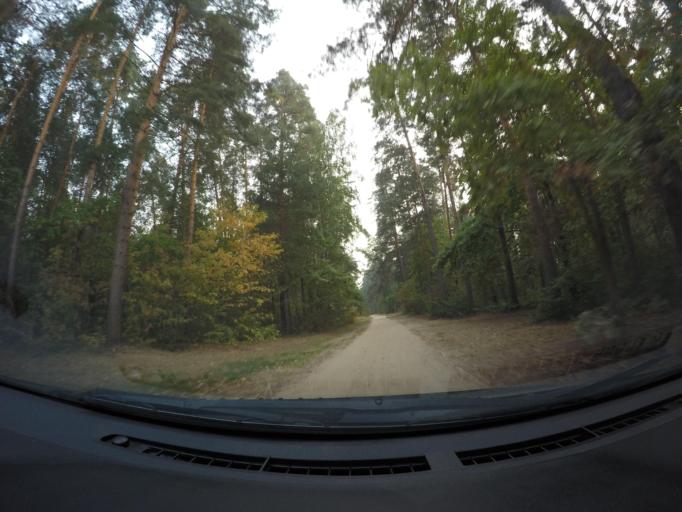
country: RU
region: Moskovskaya
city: Imeni Tsyurupy
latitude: 55.5059
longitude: 38.6936
